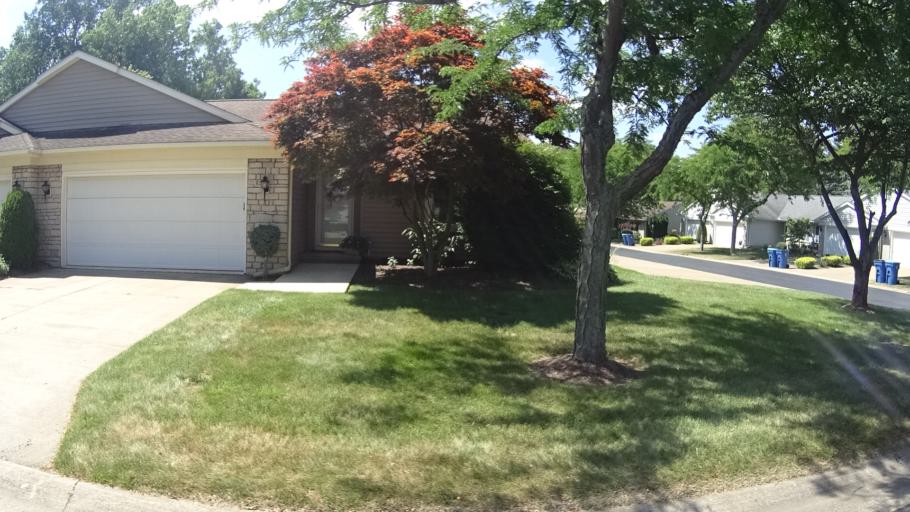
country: US
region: Ohio
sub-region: Erie County
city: Huron
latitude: 41.3823
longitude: -82.5646
